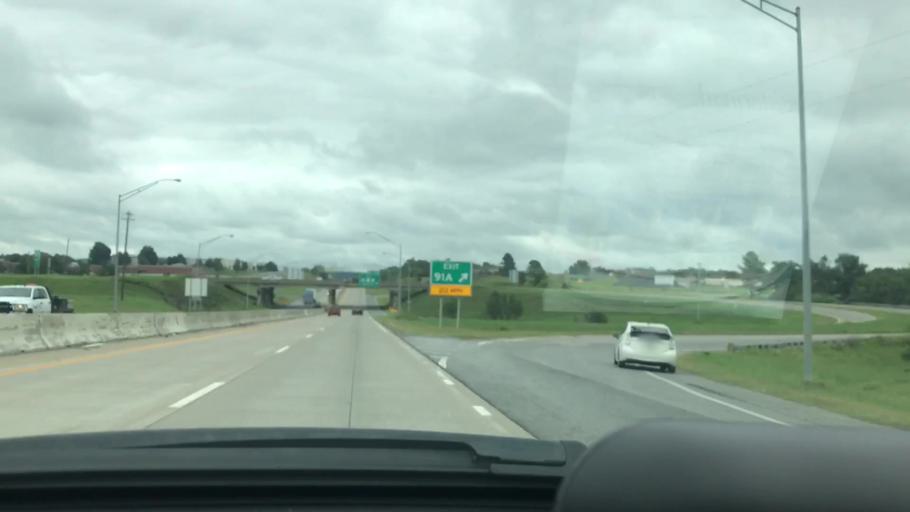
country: US
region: Oklahoma
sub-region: Pittsburg County
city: Krebs
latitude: 34.9256
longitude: -95.7415
